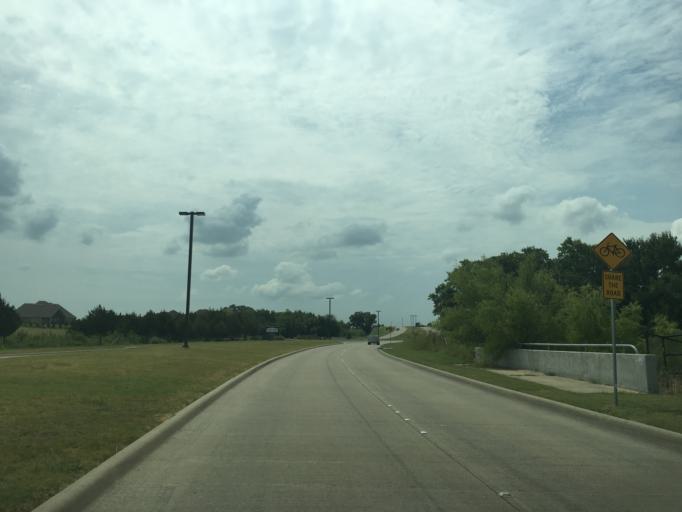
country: US
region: Texas
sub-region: Rockwall County
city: Rockwall
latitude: 32.9787
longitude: -96.4606
